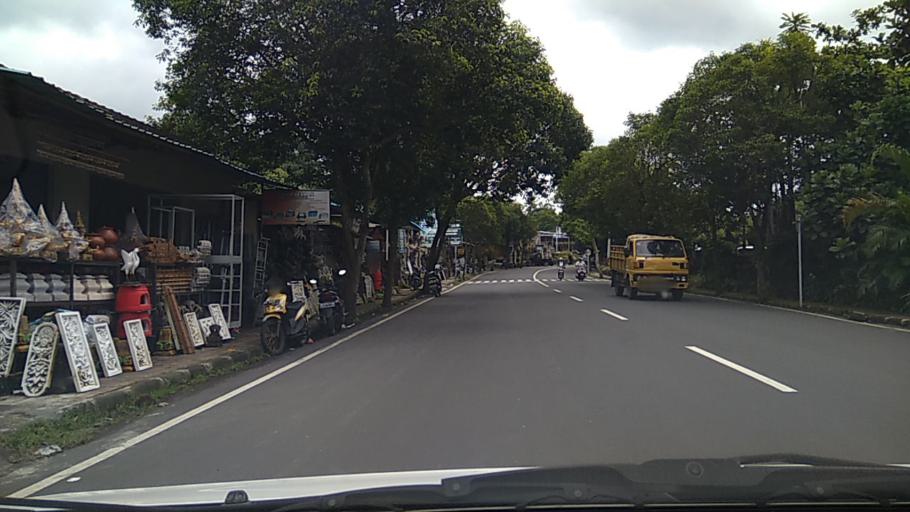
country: ID
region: Bali
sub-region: Kabupaten Gianyar
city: Ubud
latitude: -8.5227
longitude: 115.2876
